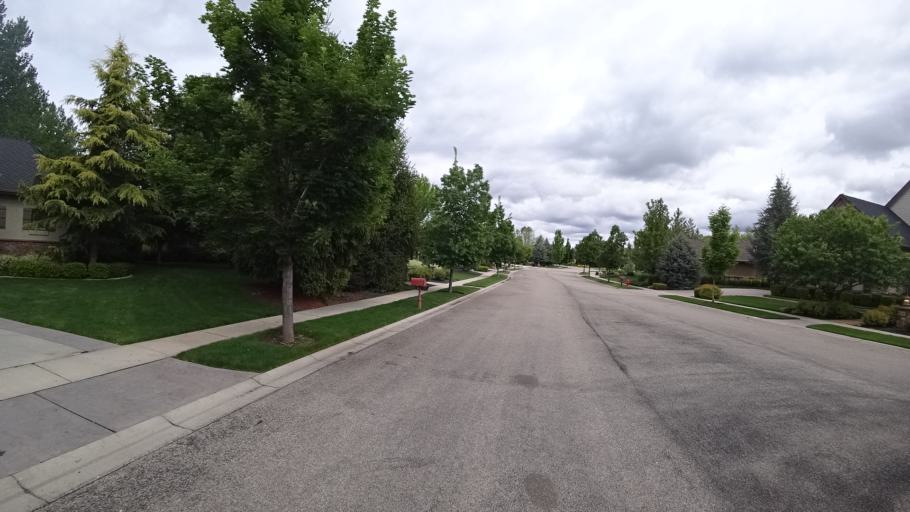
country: US
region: Idaho
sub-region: Ada County
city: Eagle
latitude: 43.6786
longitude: -116.3616
